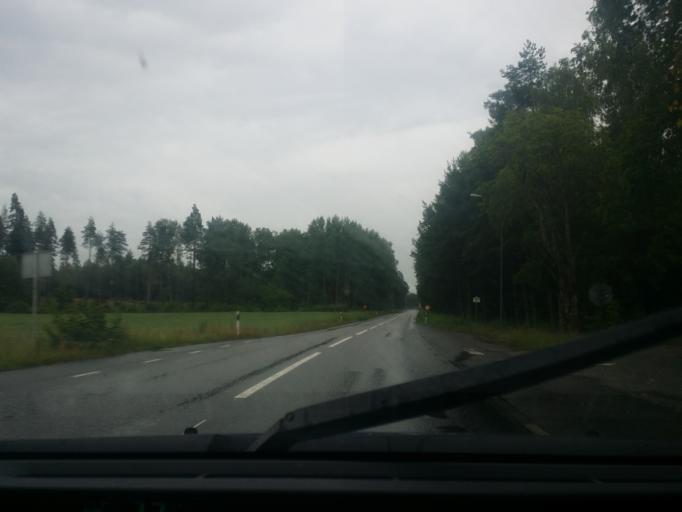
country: SE
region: OErebro
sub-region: Lindesbergs Kommun
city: Fellingsbro
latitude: 59.4165
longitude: 15.7111
